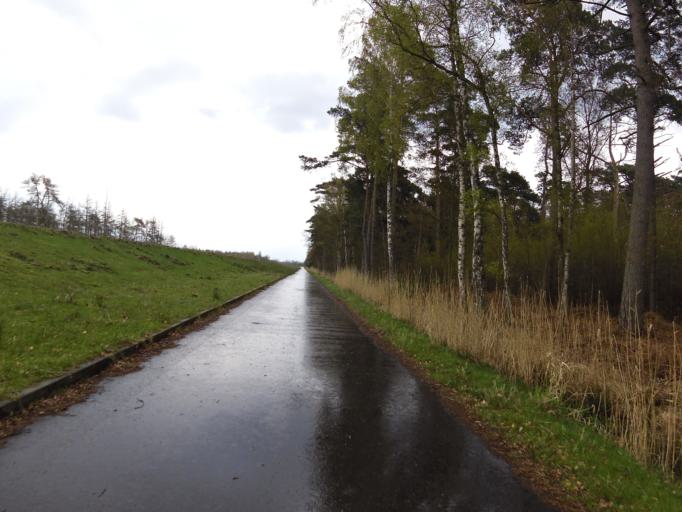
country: DE
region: Mecklenburg-Vorpommern
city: Barth
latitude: 54.4360
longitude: 12.7815
